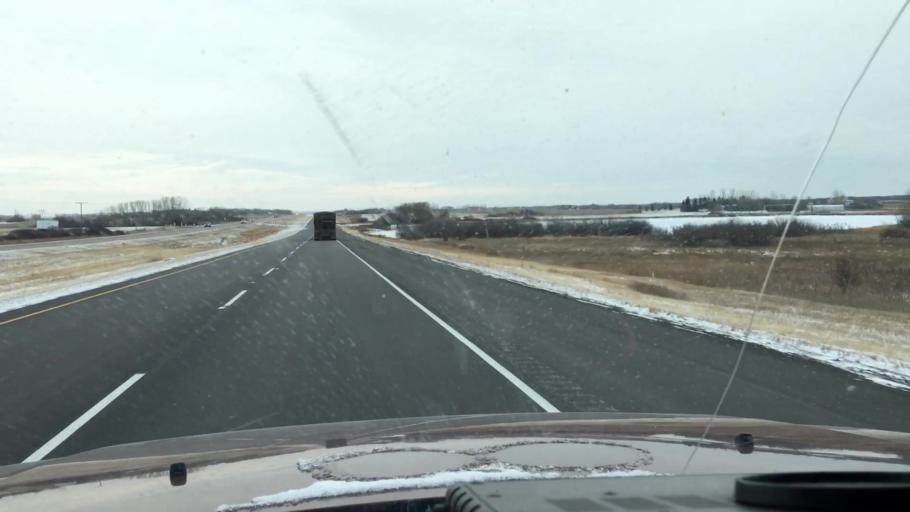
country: CA
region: Saskatchewan
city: Saskatoon
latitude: 51.9247
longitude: -106.5329
